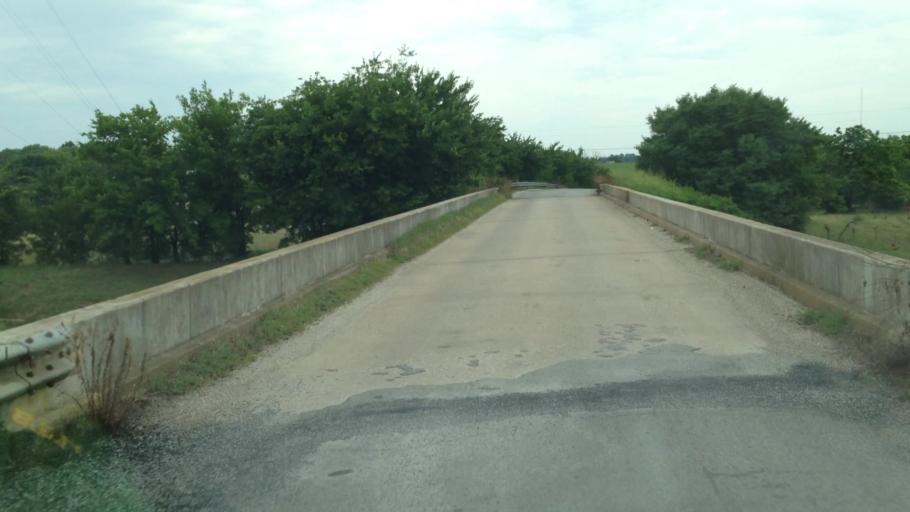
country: US
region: Oklahoma
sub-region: Craig County
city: Vinita
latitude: 36.6381
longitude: -95.1252
